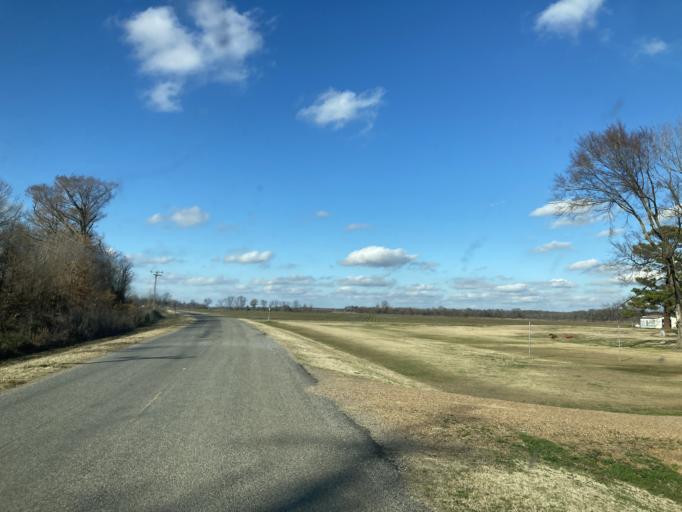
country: US
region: Mississippi
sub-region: Yazoo County
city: Yazoo City
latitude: 32.9340
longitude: -90.4732
